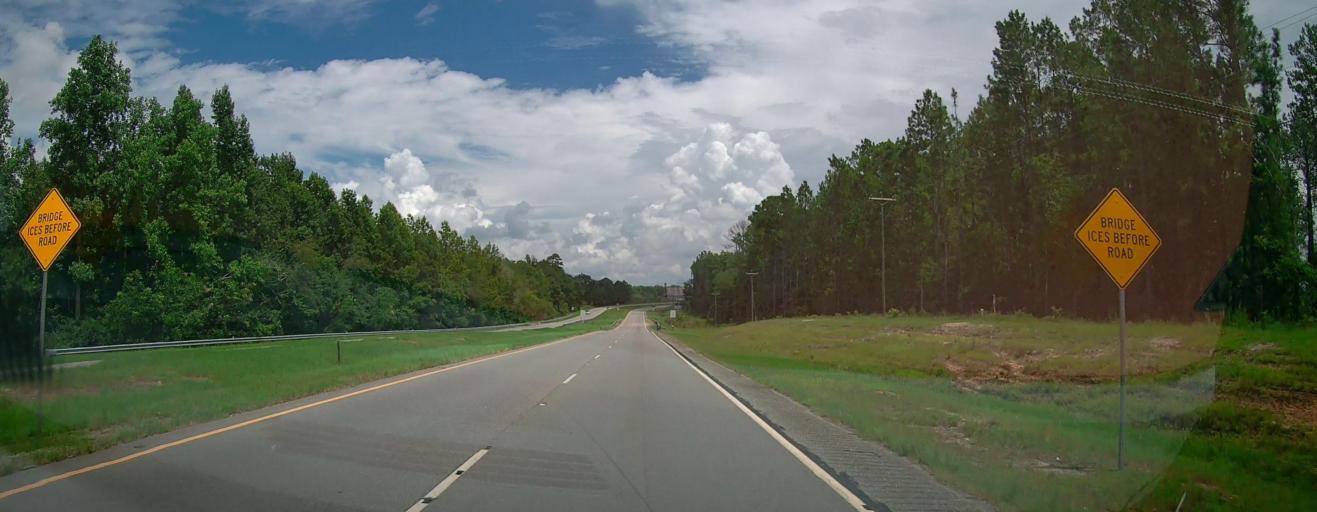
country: US
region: Georgia
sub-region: Dodge County
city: Eastman
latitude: 32.1978
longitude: -83.2191
